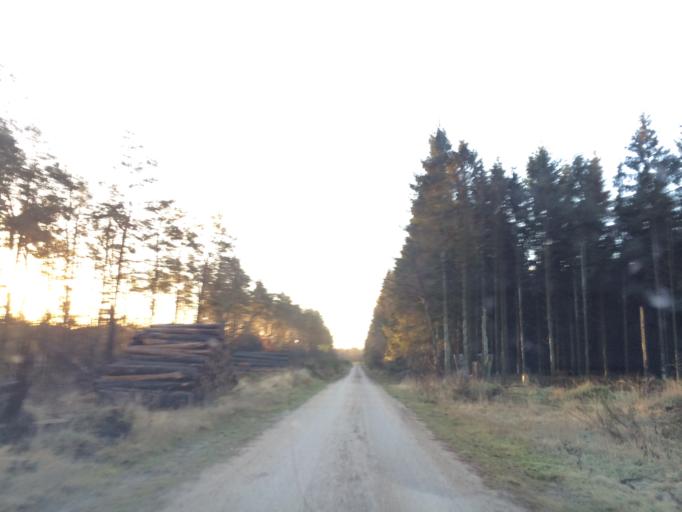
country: DK
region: Central Jutland
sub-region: Holstebro Kommune
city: Ulfborg
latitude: 56.2313
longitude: 8.4914
